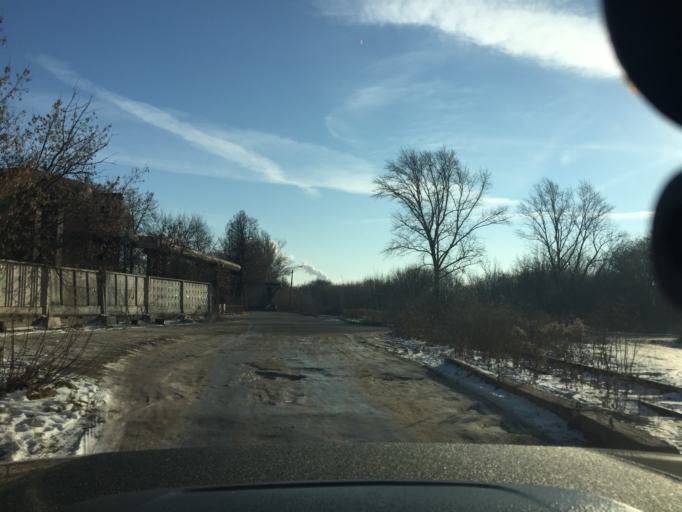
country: RU
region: Tula
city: Tula
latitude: 54.1763
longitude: 37.7014
